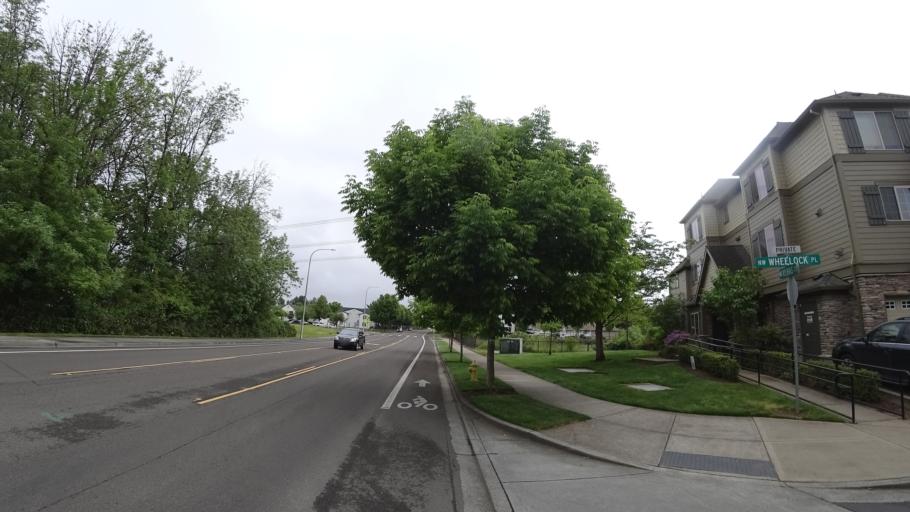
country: US
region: Oregon
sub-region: Washington County
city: Rockcreek
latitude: 45.5271
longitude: -122.8956
